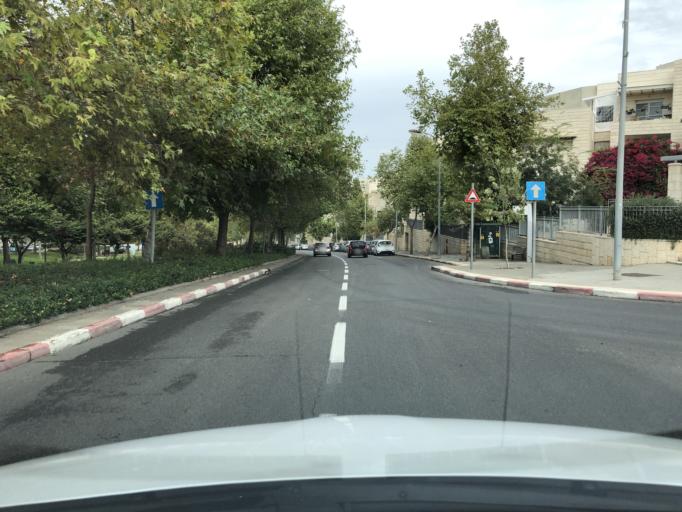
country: IL
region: Central District
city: Modiin
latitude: 31.9157
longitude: 35.0046
